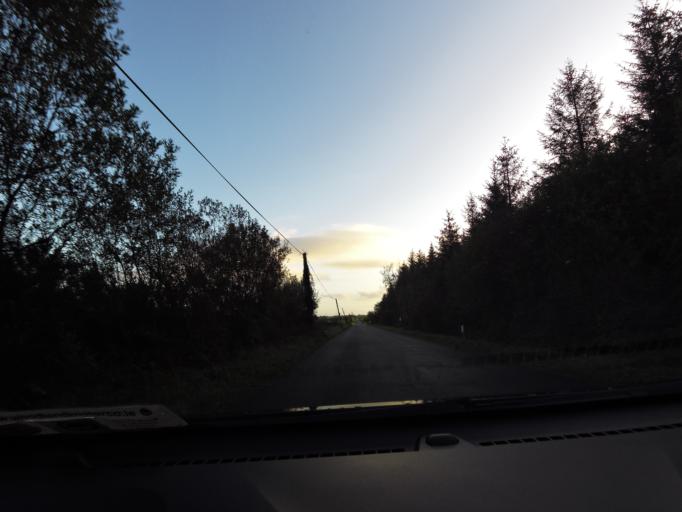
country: IE
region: Connaught
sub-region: Roscommon
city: Castlerea
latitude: 53.6542
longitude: -8.6027
